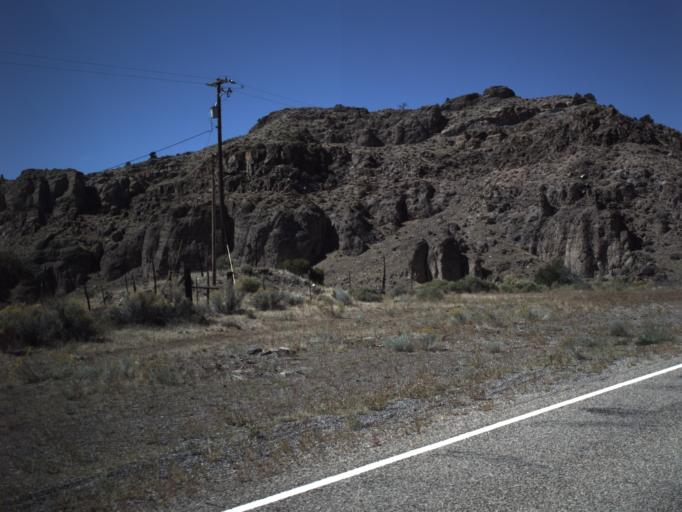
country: US
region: Utah
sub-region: Piute County
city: Junction
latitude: 38.1977
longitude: -112.1502
